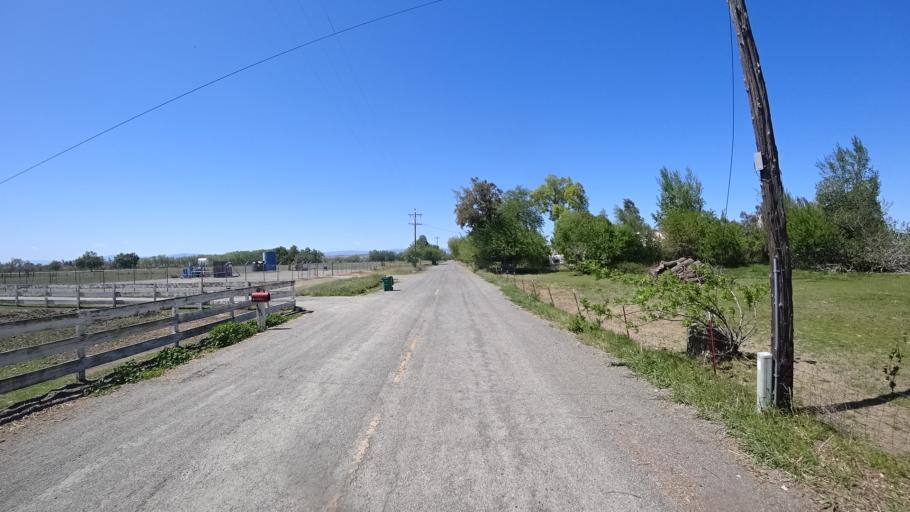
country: US
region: California
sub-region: Glenn County
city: Orland
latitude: 39.7951
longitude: -122.2445
